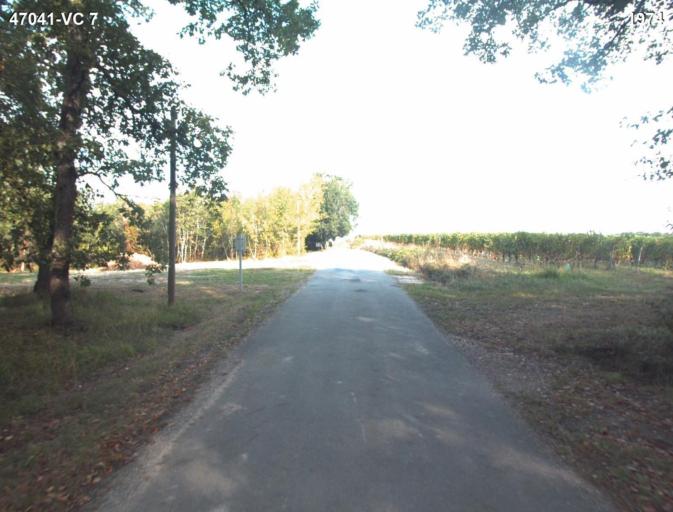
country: FR
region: Aquitaine
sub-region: Departement du Lot-et-Garonne
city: Port-Sainte-Marie
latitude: 44.1933
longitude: 0.4203
